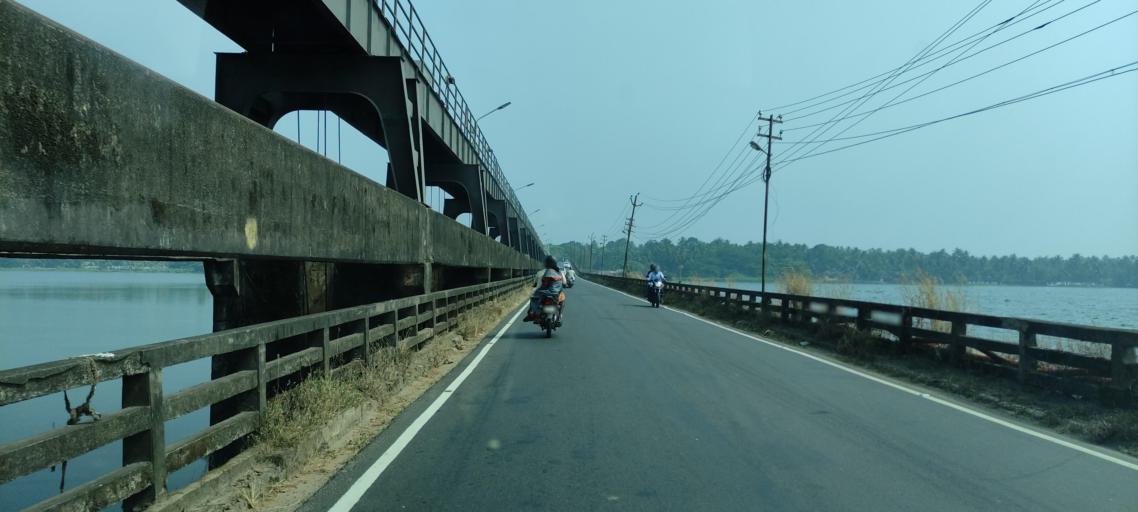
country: IN
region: Kerala
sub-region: Alappuzha
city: Shertallai
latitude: 9.6737
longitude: 76.4033
